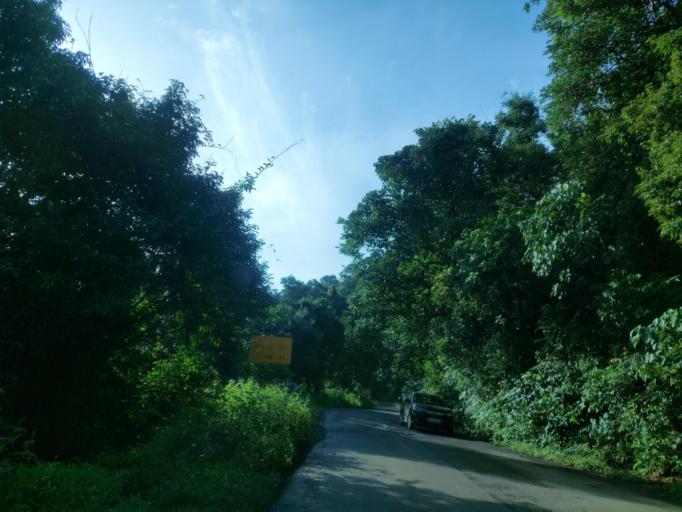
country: IN
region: Maharashtra
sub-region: Sindhudurg
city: Savantvadi
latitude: 15.9360
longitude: 73.9735
